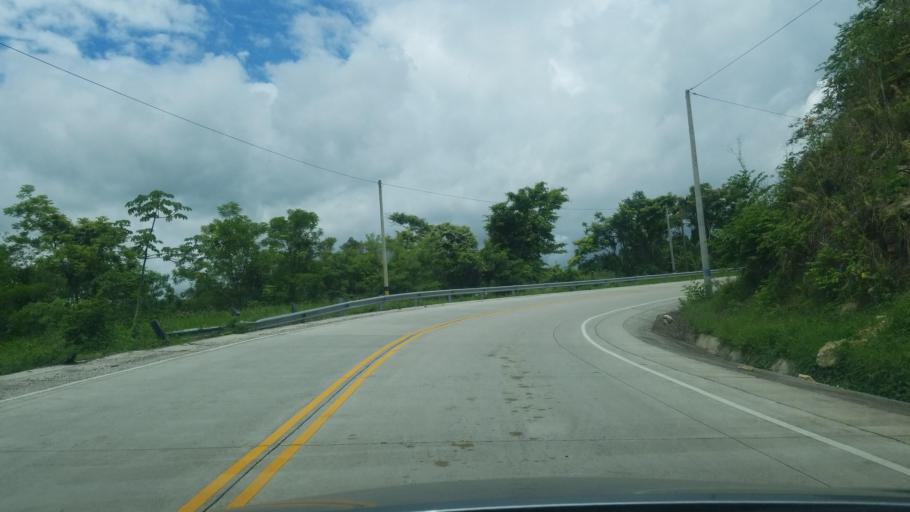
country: HN
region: Copan
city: Florida
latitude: 14.9979
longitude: -88.8451
